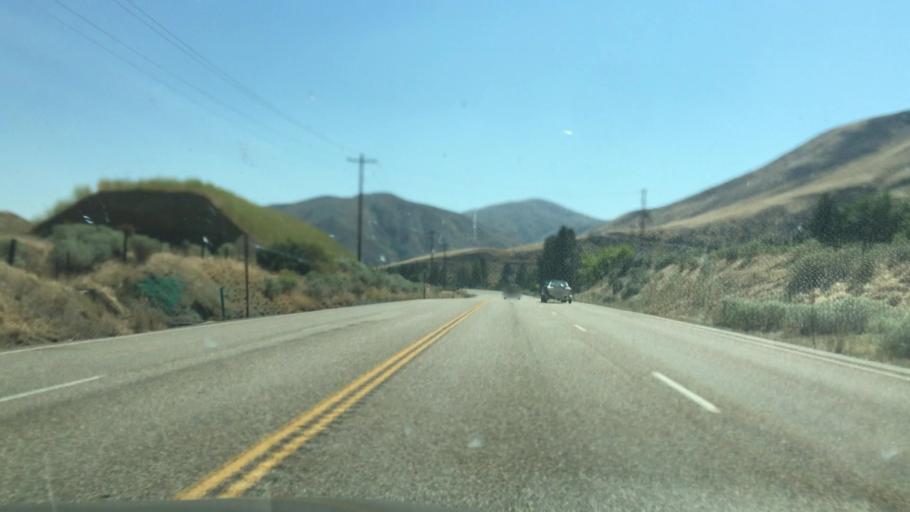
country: US
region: Idaho
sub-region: Gem County
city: Emmett
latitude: 43.9973
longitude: -116.1844
